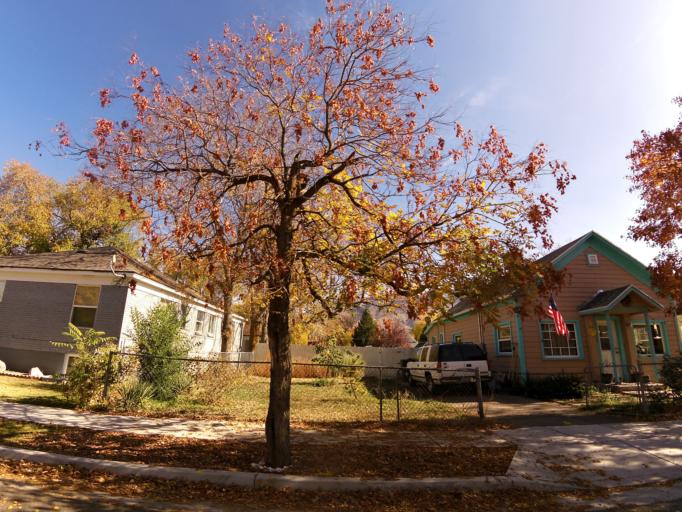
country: US
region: Utah
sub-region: Weber County
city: Ogden
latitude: 41.2303
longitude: -111.9635
